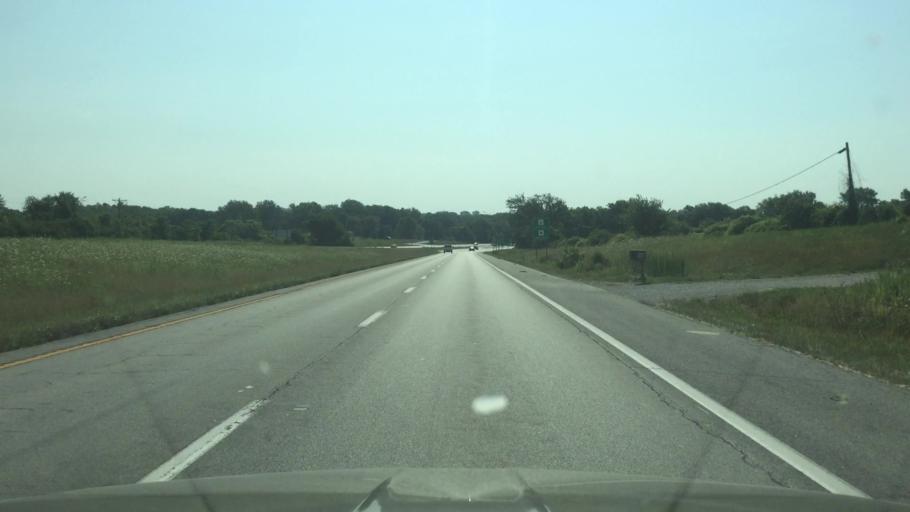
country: US
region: Missouri
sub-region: Jackson County
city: Lone Jack
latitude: 38.8683
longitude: -94.0650
